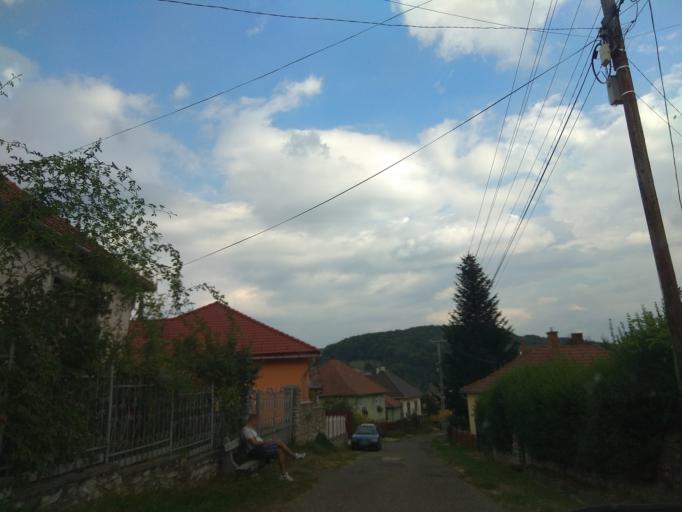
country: HU
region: Borsod-Abauj-Zemplen
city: Saly
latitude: 48.0695
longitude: 20.6284
